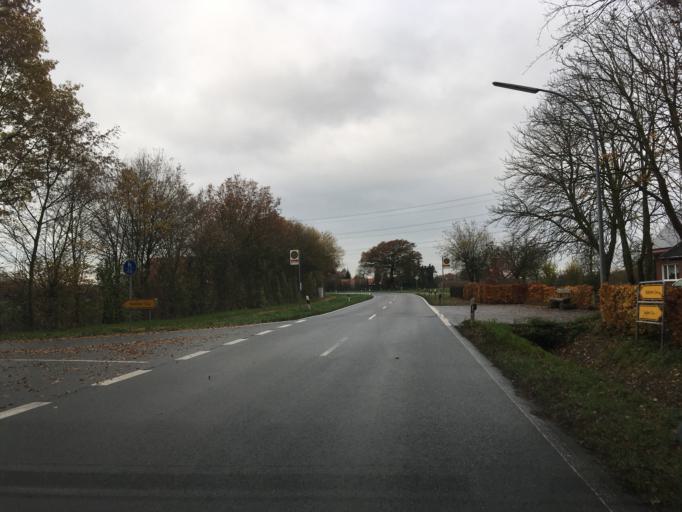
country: DE
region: North Rhine-Westphalia
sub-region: Regierungsbezirk Munster
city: Gescher
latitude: 51.9872
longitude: 6.9737
